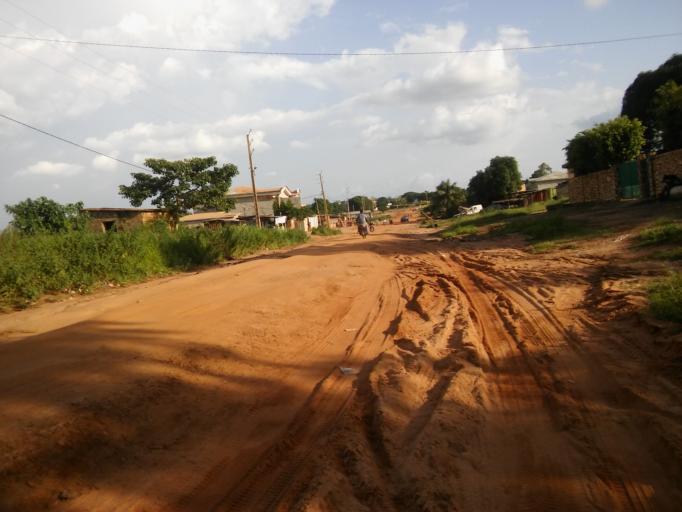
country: BJ
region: Borgou
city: Parakou
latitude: 9.3555
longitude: 2.6374
